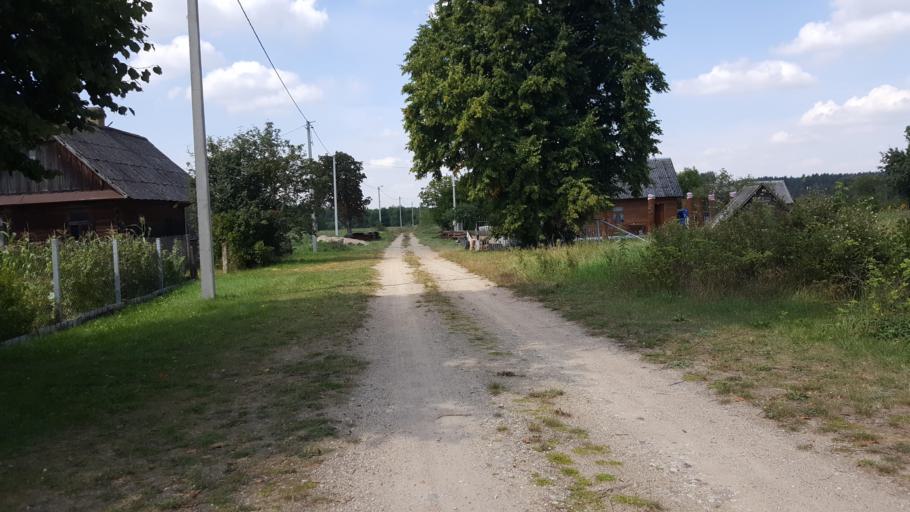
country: PL
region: Podlasie
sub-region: Powiat hajnowski
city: Hajnowka
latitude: 52.5736
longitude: 23.5524
